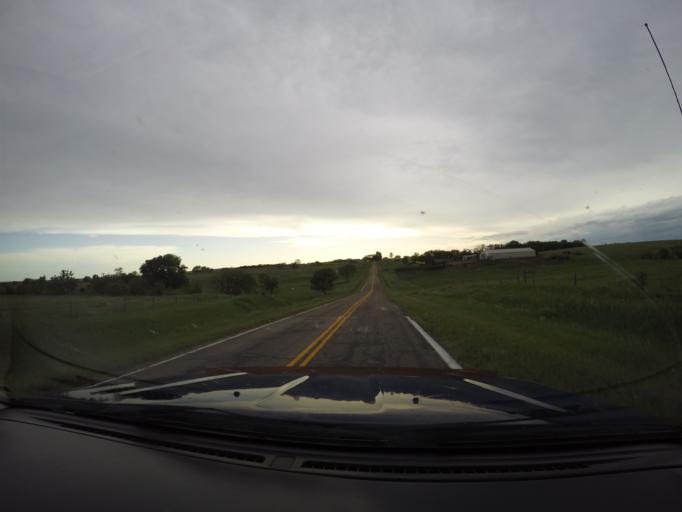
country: US
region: Kansas
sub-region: Smith County
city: Smith Center
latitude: 39.8282
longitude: -98.5742
